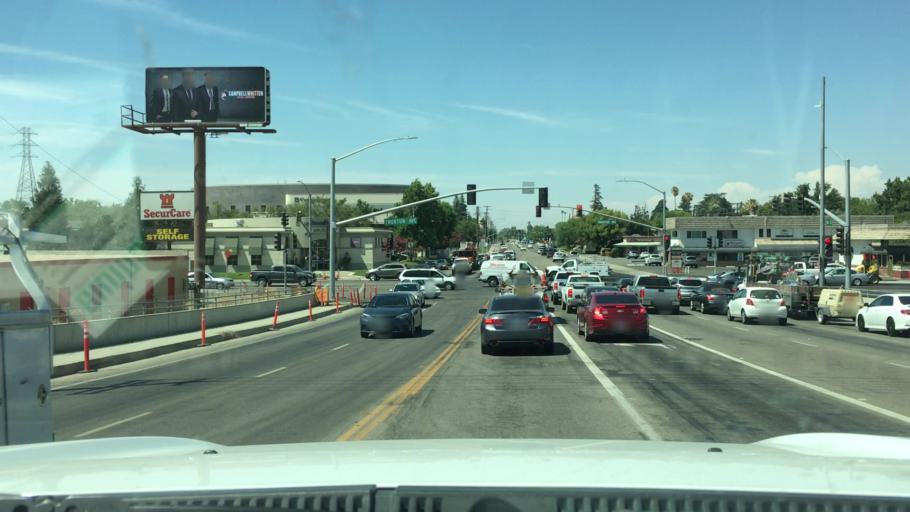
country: US
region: California
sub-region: Kern County
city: Bakersfield
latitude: 35.3728
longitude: -119.0387
